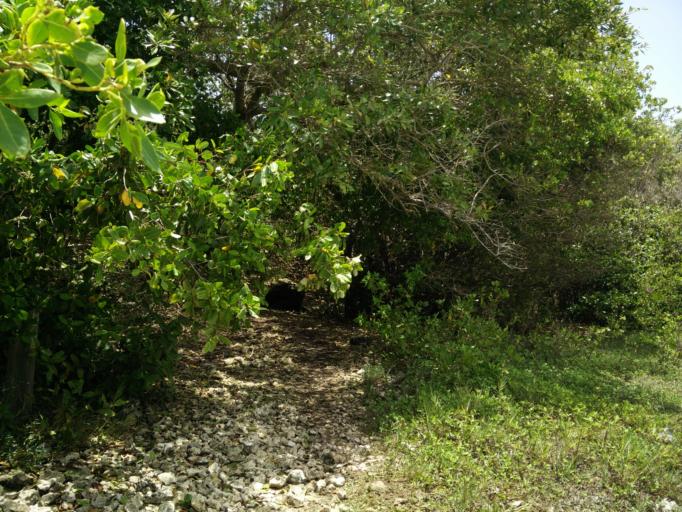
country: GP
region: Guadeloupe
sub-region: Guadeloupe
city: Sainte-Anne
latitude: 16.2413
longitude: -61.3397
